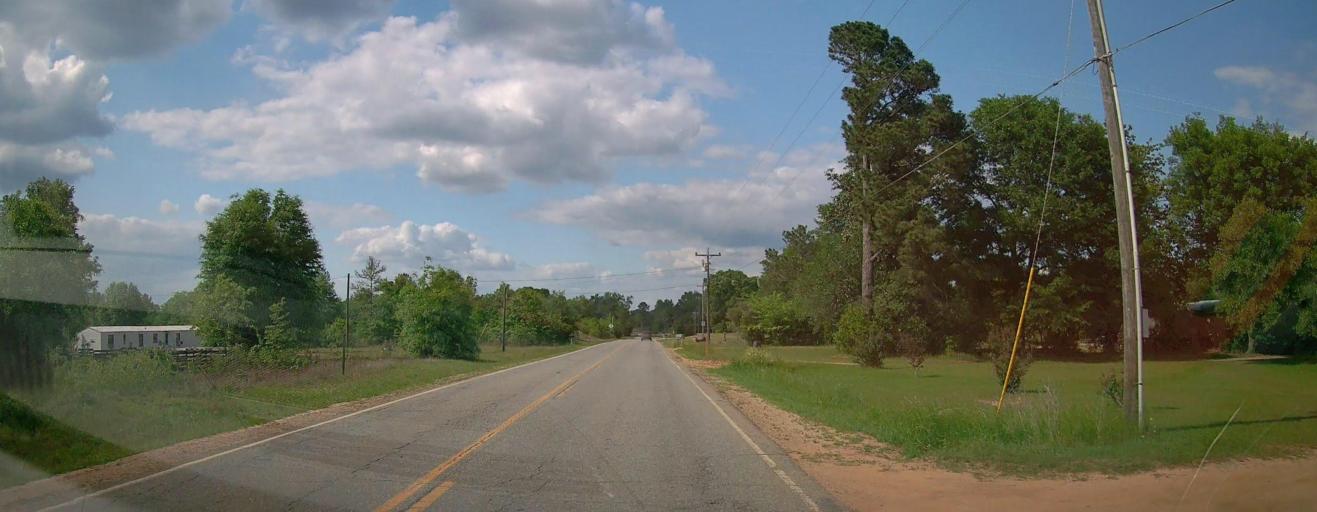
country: US
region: Georgia
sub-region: Laurens County
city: East Dublin
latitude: 32.5916
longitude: -82.8652
